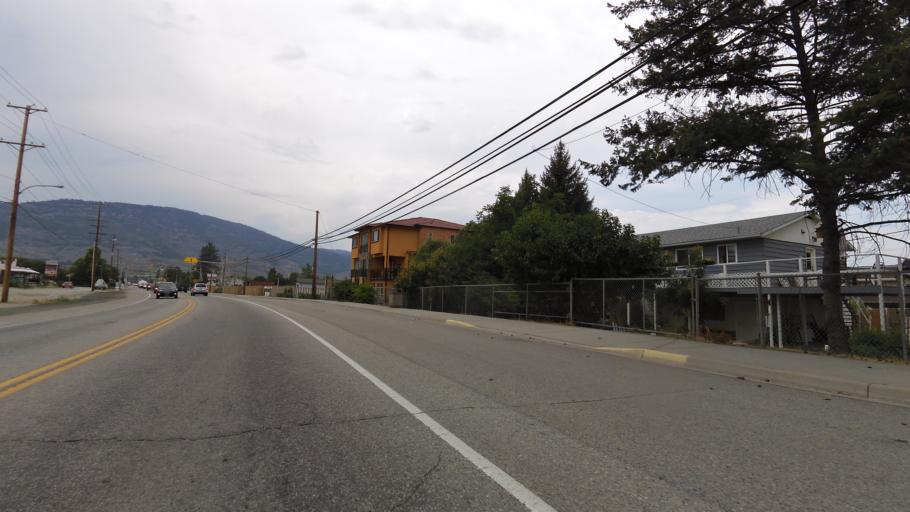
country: CA
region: British Columbia
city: Osoyoos
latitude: 49.0289
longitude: -119.4480
